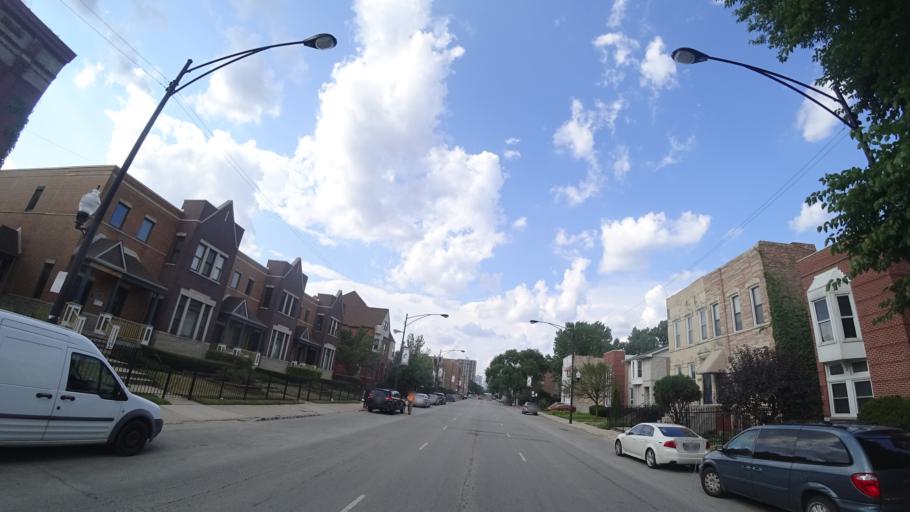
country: US
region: Illinois
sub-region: Cook County
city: Chicago
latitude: 41.8331
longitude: -87.6218
